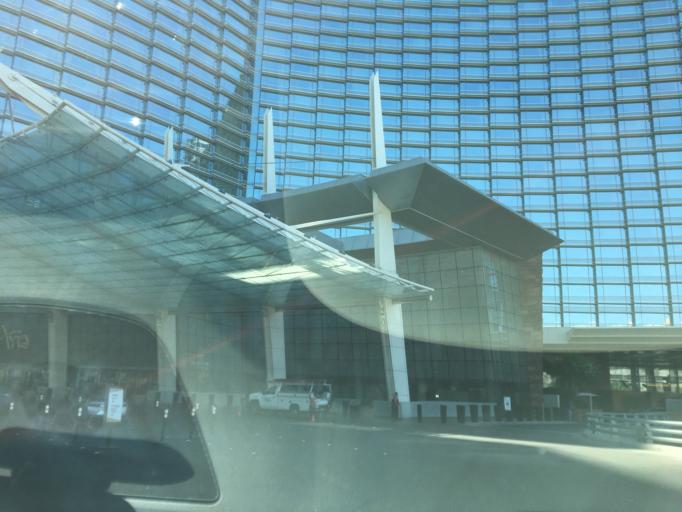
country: US
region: Nevada
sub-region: Clark County
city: Paradise
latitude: 36.1082
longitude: -115.1776
